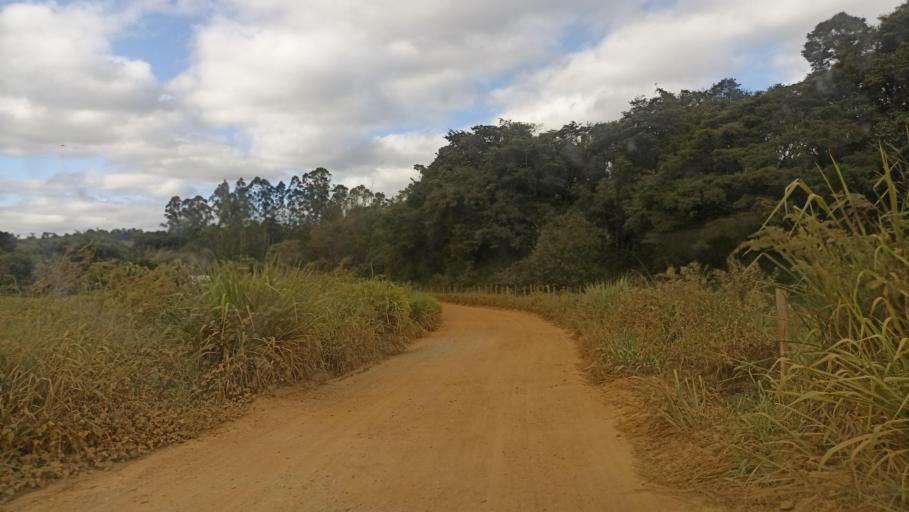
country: BR
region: Minas Gerais
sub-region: Tiradentes
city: Tiradentes
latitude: -21.0966
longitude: -44.0759
